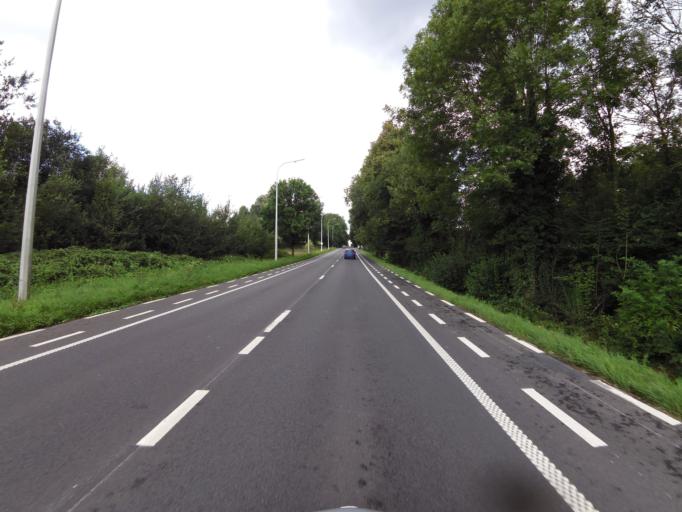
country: BE
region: Wallonia
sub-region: Province du Hainaut
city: Mons
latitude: 50.4387
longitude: 3.9898
